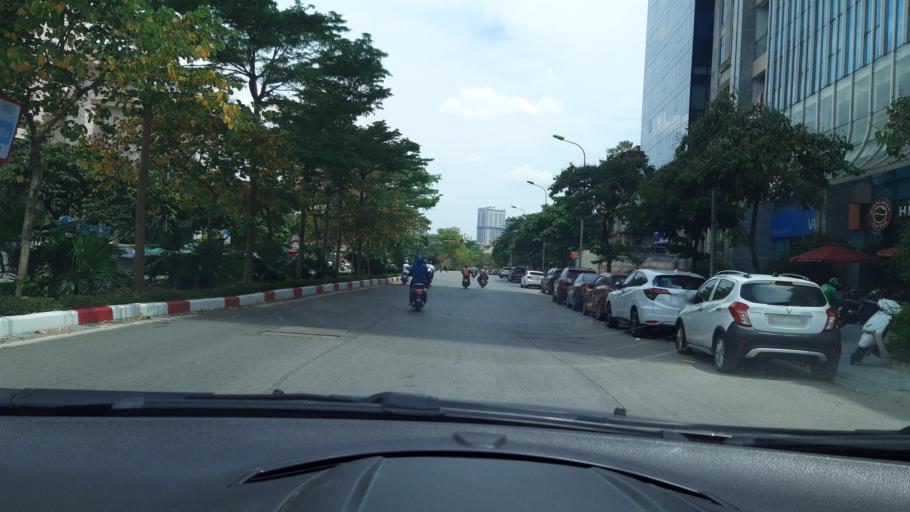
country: VN
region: Ha Noi
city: Cau Giay
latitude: 21.0413
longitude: 105.7903
